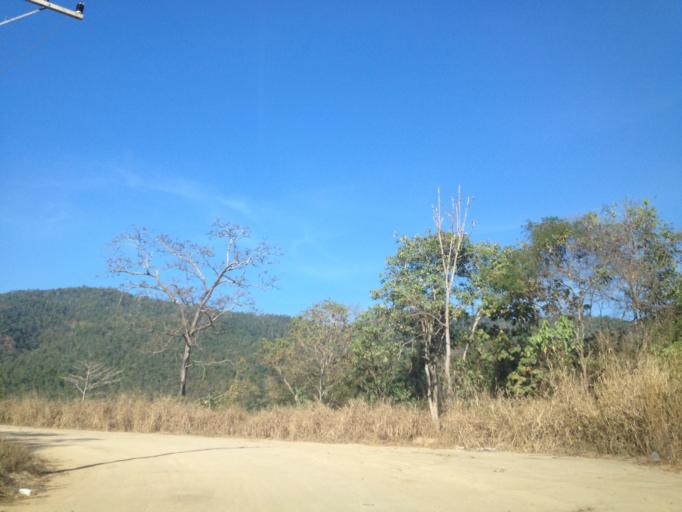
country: TH
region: Mae Hong Son
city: Ban Huai I Huak
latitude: 18.0779
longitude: 98.1897
